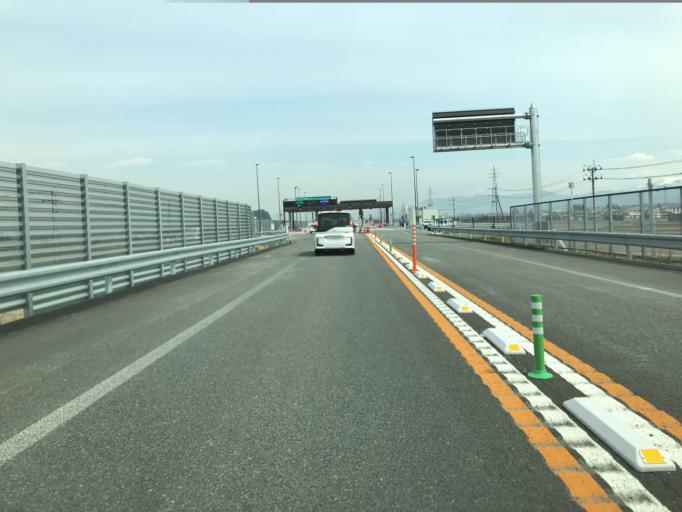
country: JP
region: Yamagata
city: Yonezawa
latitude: 37.9575
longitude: 140.1175
